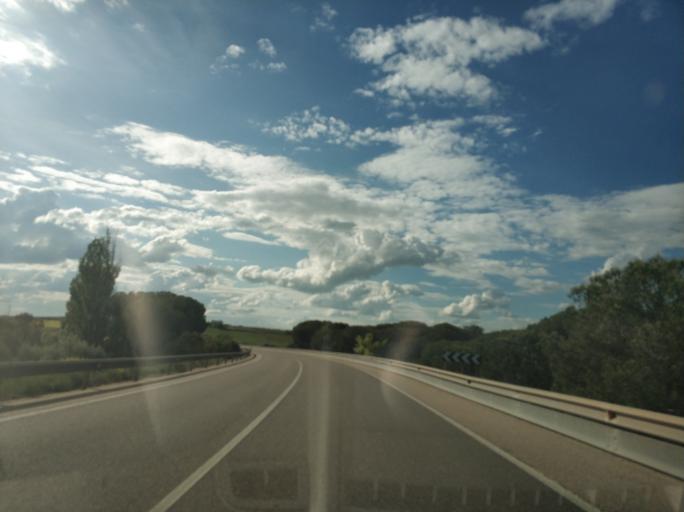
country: ES
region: Castille and Leon
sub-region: Provincia de Valladolid
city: Penafiel
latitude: 41.6067
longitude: -4.1413
